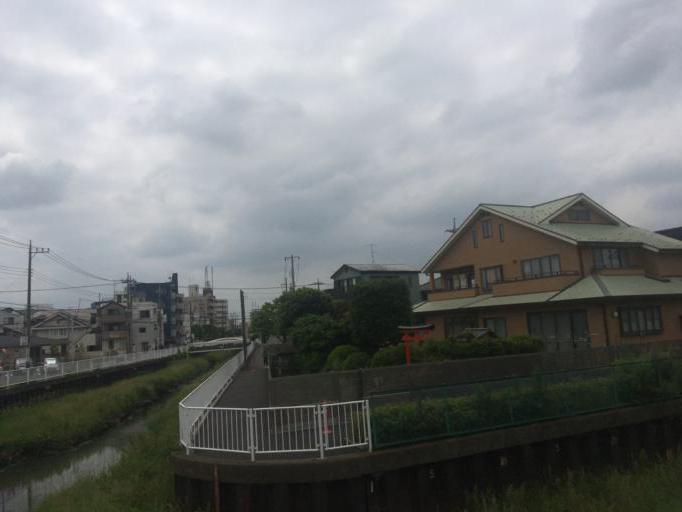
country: JP
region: Saitama
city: Kawaguchi
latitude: 35.8299
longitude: 139.7063
